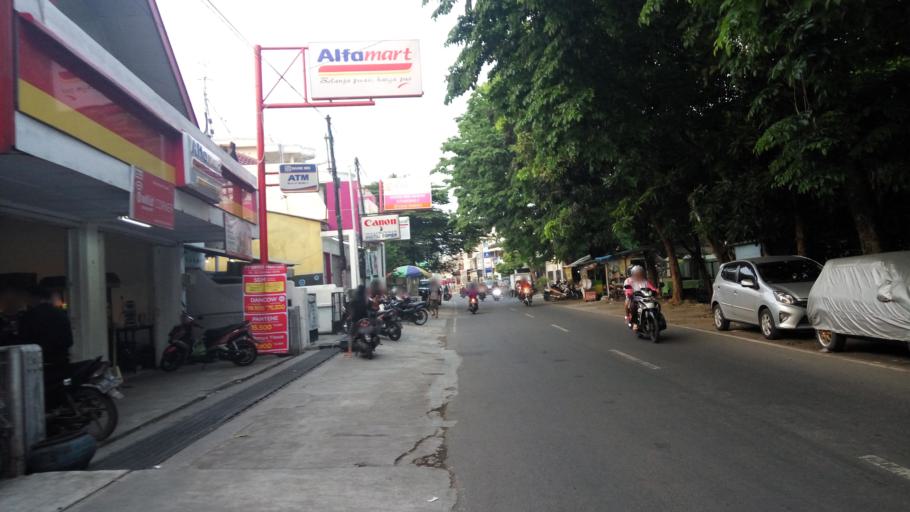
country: ID
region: Central Java
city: Semarang
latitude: -6.9894
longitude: 110.4040
